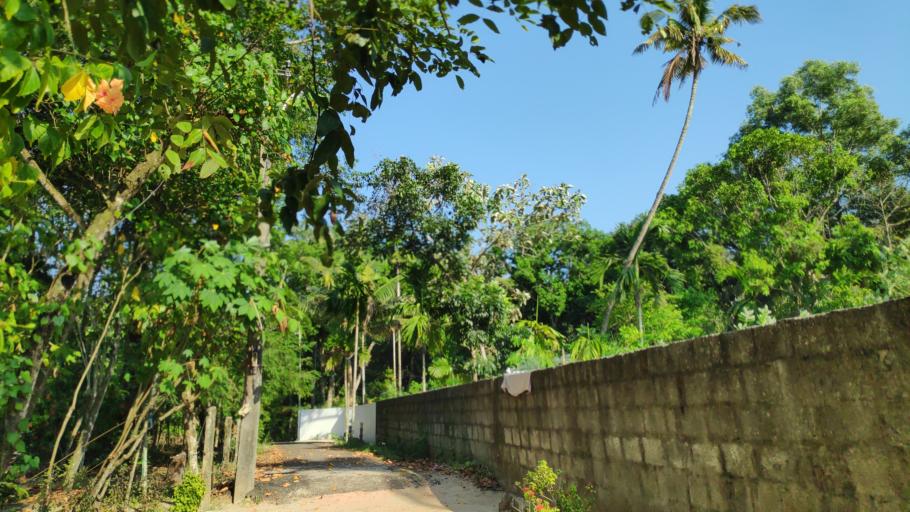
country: IN
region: Kerala
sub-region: Alappuzha
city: Alleppey
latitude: 9.5462
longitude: 76.3080
